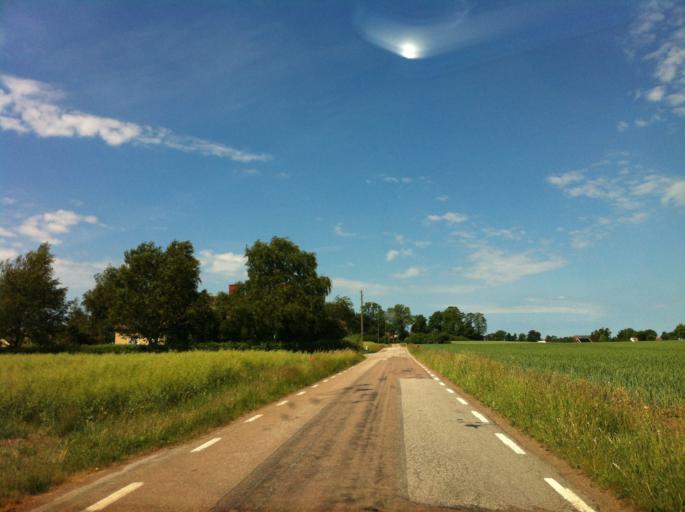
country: SE
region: Skane
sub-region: Helsingborg
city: Glumslov
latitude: 55.9417
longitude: 12.8839
